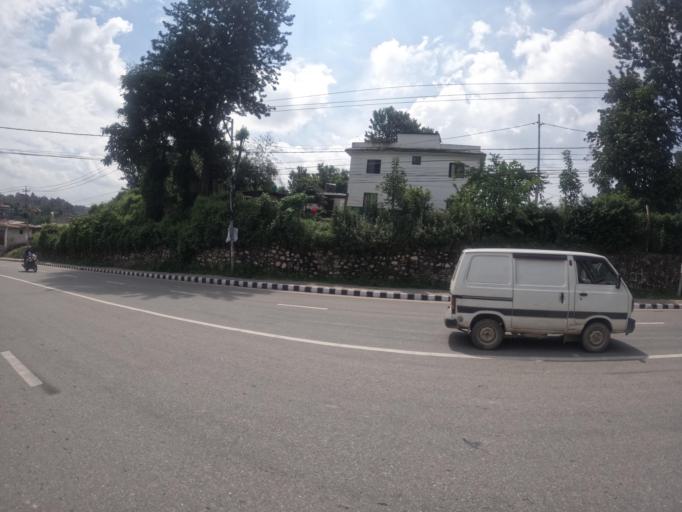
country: NP
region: Central Region
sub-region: Bagmati Zone
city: Bhaktapur
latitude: 27.6820
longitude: 85.3800
